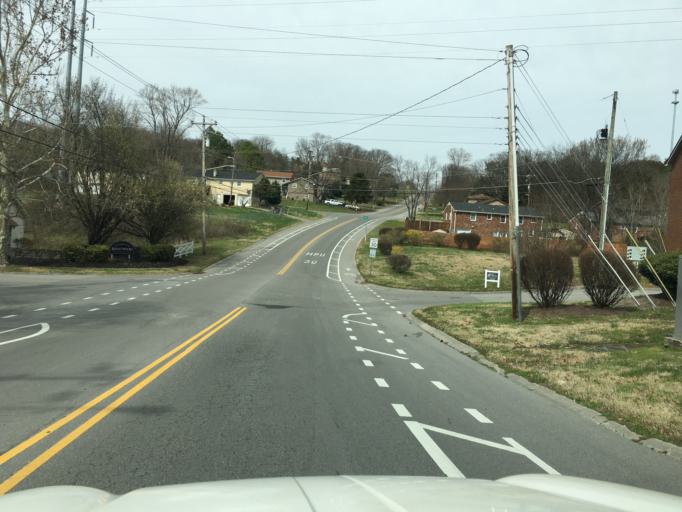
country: US
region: Tennessee
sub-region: Williamson County
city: Brentwood Estates
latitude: 36.0454
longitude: -86.7252
